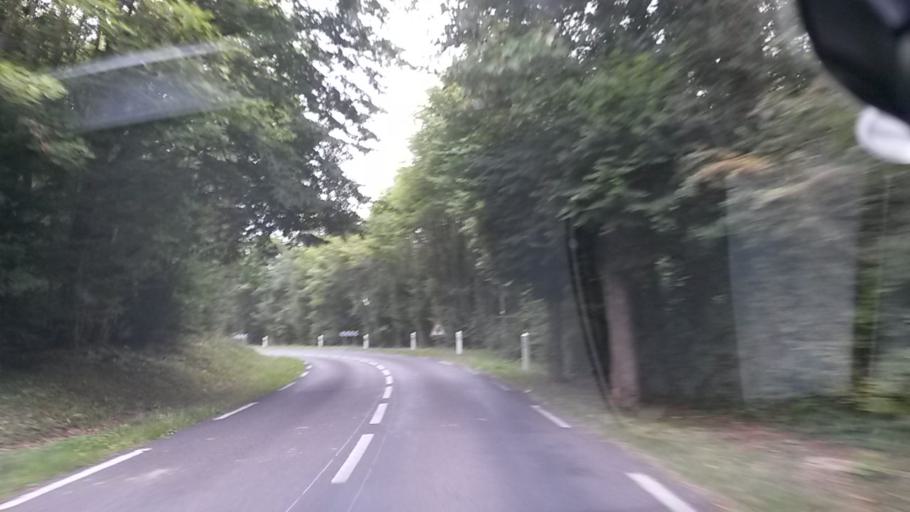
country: FR
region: Haute-Normandie
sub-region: Departement de la Seine-Maritime
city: La Feuillie
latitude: 49.3966
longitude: 1.4722
